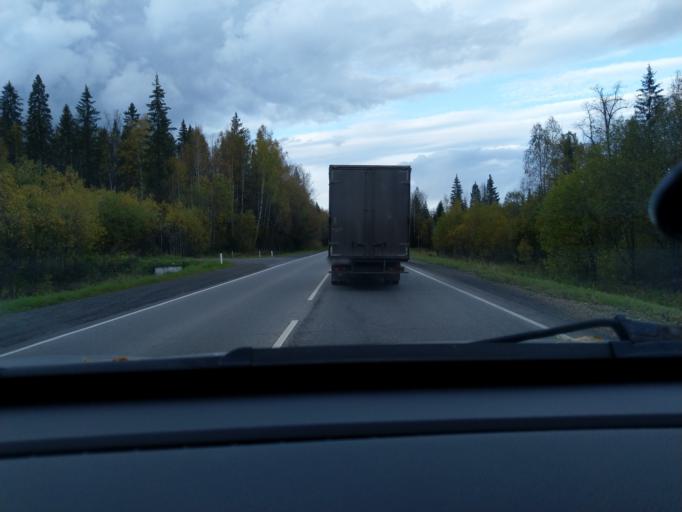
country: RU
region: Perm
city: Dobryanka
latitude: 58.4081
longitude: 56.5147
